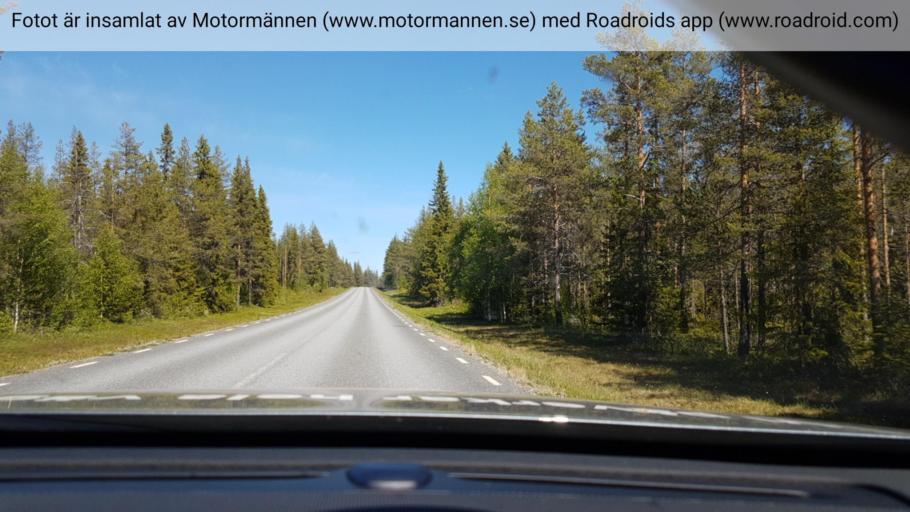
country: SE
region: Vaesterbotten
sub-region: Vilhelmina Kommun
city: Vilhelmina
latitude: 64.6393
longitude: 16.9454
